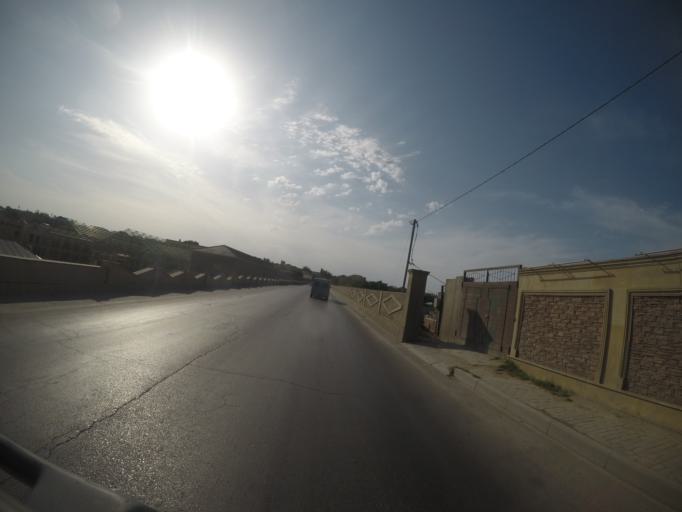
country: AZ
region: Baki
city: Binagadi
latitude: 40.4691
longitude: 49.8400
